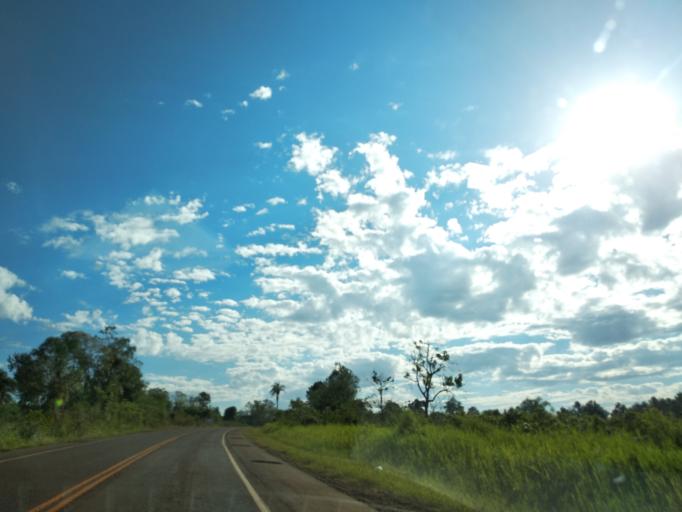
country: AR
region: Misiones
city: Ruiz de Montoya
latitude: -27.0591
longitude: -55.0399
